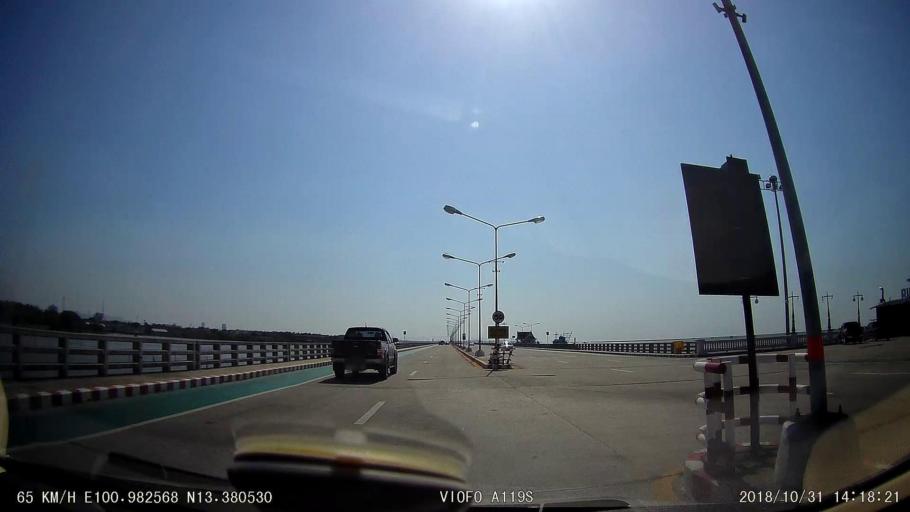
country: TH
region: Chon Buri
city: Chon Buri
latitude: 13.3803
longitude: 100.9823
